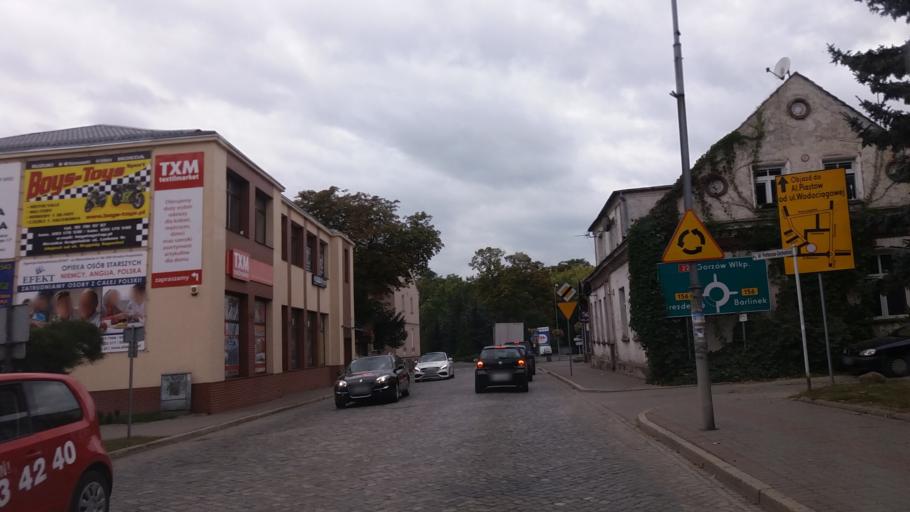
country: PL
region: Lubusz
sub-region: Powiat strzelecko-drezdenecki
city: Strzelce Krajenskie
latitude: 52.8778
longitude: 15.5307
